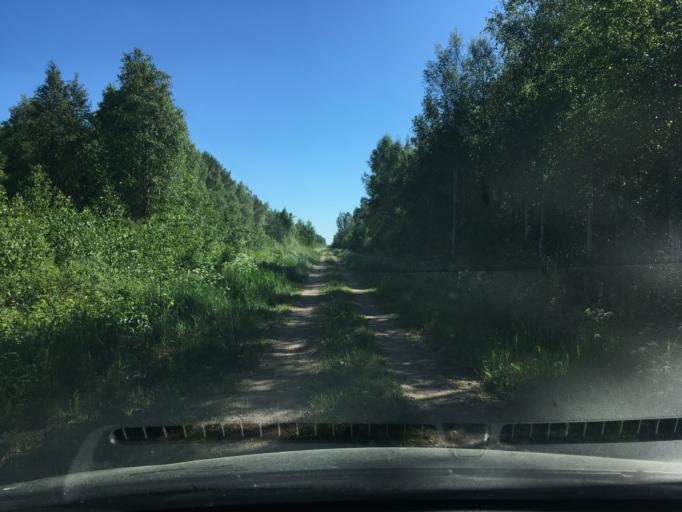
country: EE
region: Laeaene
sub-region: Lihula vald
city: Lihula
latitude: 58.6316
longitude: 23.7429
